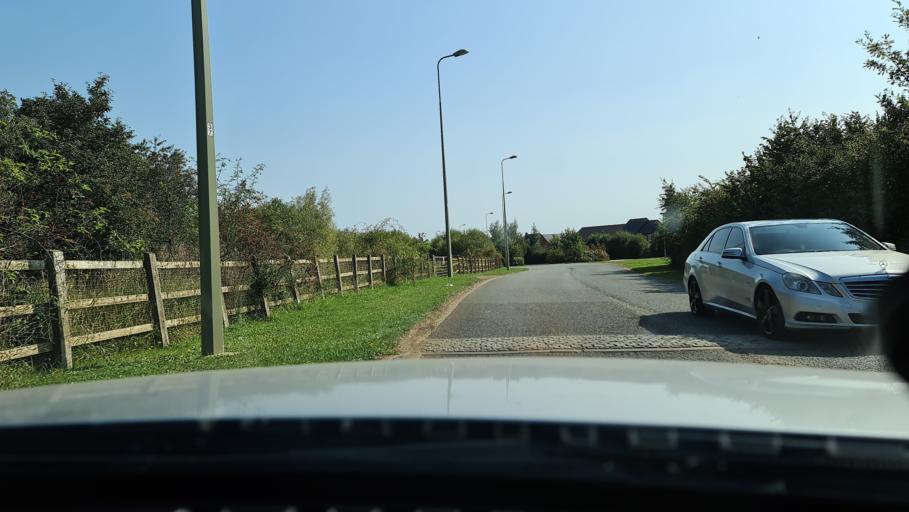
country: GB
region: England
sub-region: Oxfordshire
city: Hanwell
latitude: 52.0803
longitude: -1.3561
